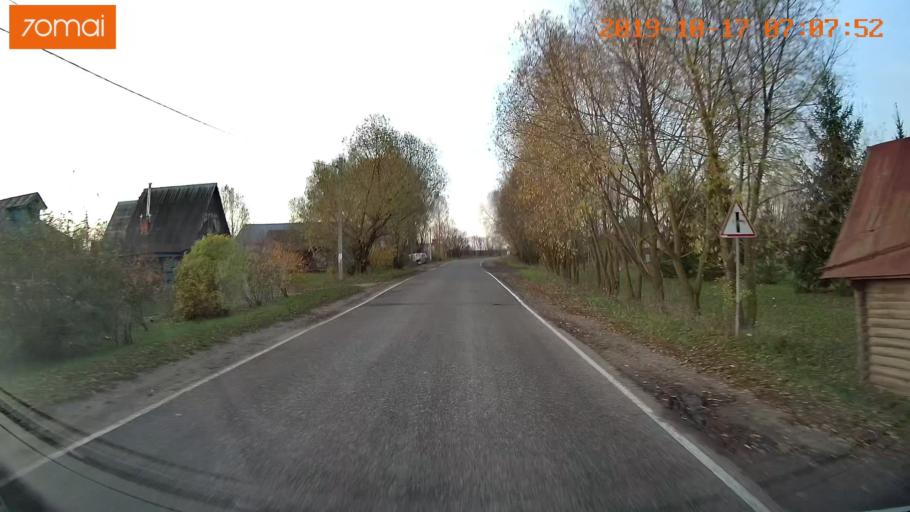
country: RU
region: Vladimir
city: Suzdal'
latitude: 56.4251
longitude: 40.4154
